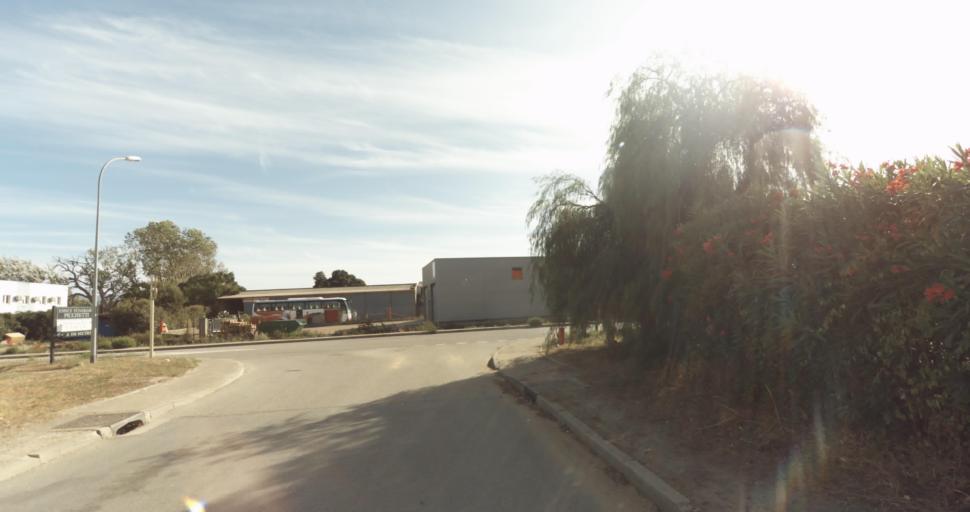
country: FR
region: Corsica
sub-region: Departement de la Corse-du-Sud
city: Afa
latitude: 41.9298
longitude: 8.7895
